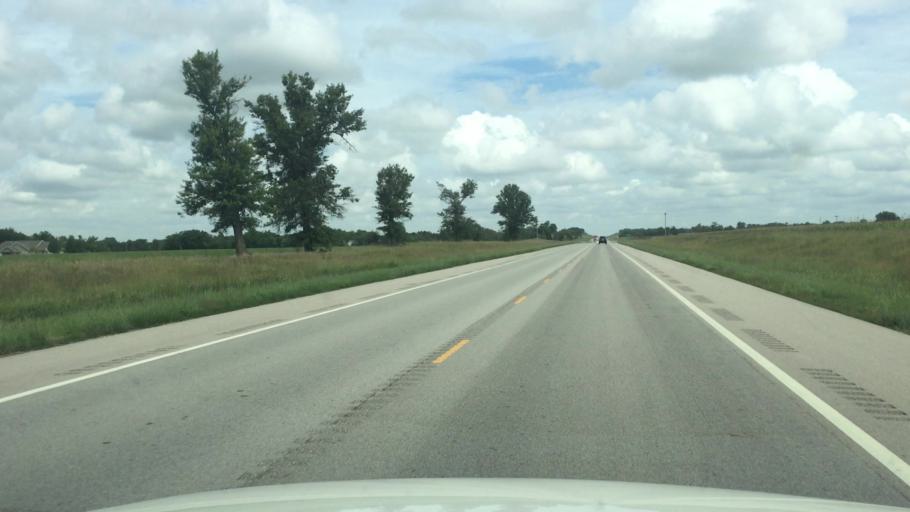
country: US
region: Kansas
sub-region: Allen County
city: Iola
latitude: 37.9908
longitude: -95.3809
